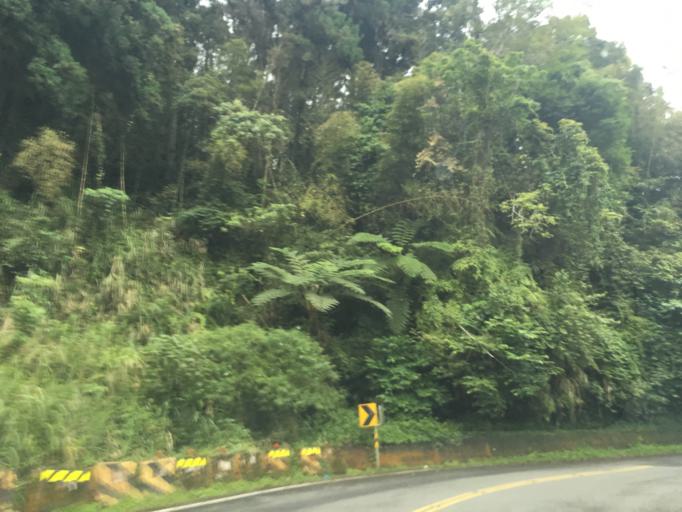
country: TW
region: Taiwan
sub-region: Chiayi
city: Jiayi Shi
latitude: 23.4898
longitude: 120.6991
